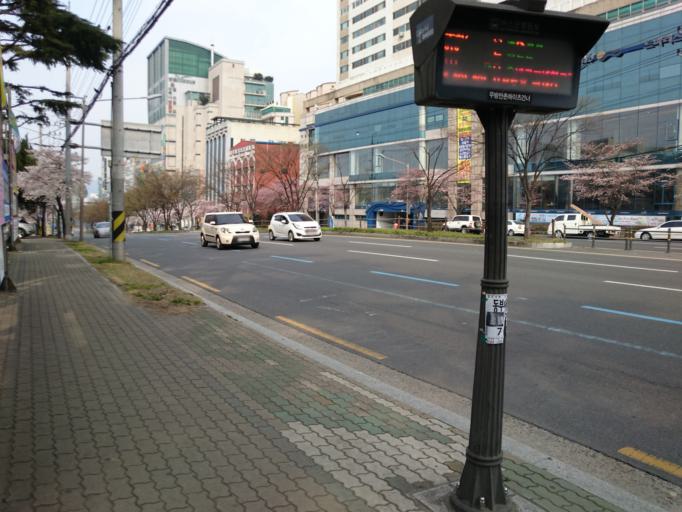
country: KR
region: Daegu
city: Daegu
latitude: 35.8687
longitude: 128.6313
